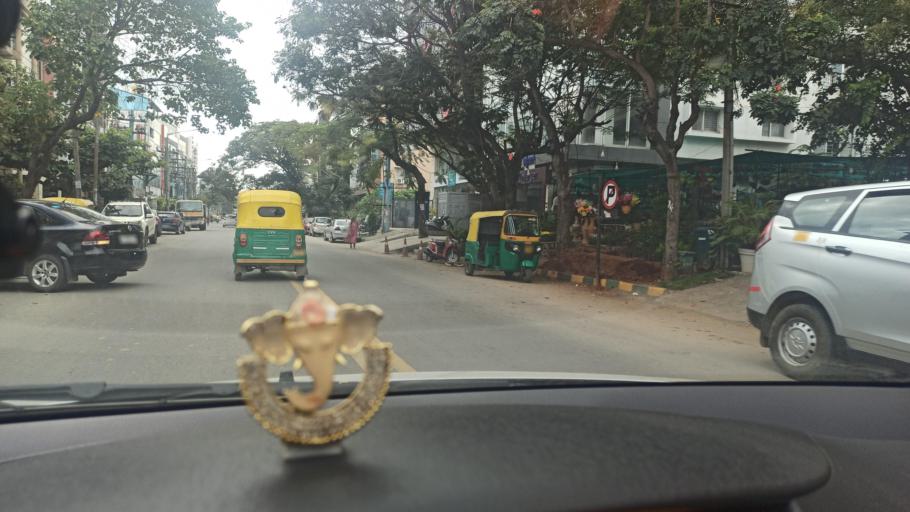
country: IN
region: Karnataka
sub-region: Bangalore Urban
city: Bangalore
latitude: 12.9114
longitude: 77.6324
